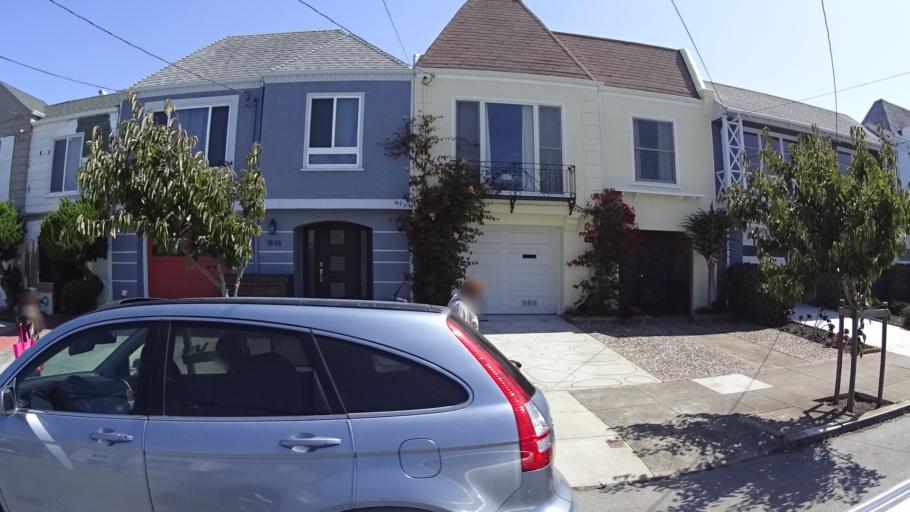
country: US
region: California
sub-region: San Mateo County
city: Daly City
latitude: 37.7528
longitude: -122.4860
